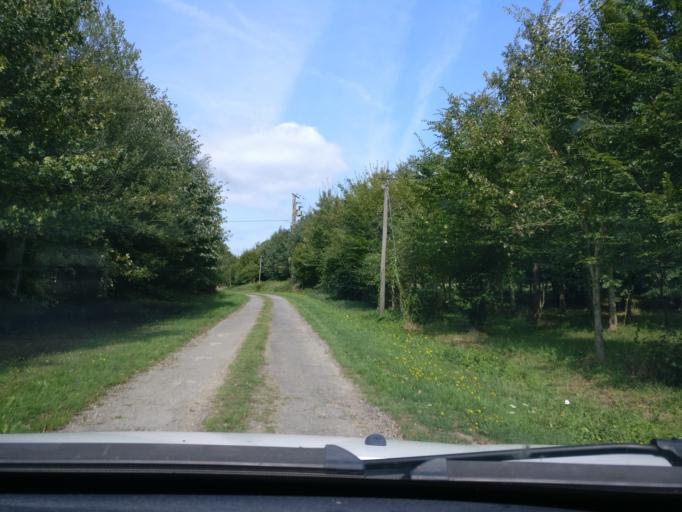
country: FR
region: Brittany
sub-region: Departement d'Ille-et-Vilaine
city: Gosne
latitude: 48.2612
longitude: -1.4851
